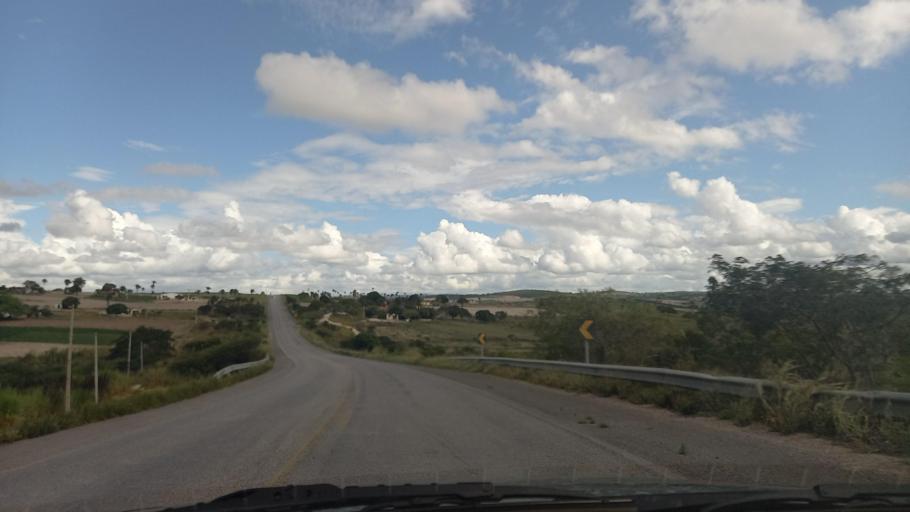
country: BR
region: Pernambuco
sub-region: Lajedo
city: Lajedo
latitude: -8.7280
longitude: -36.4317
